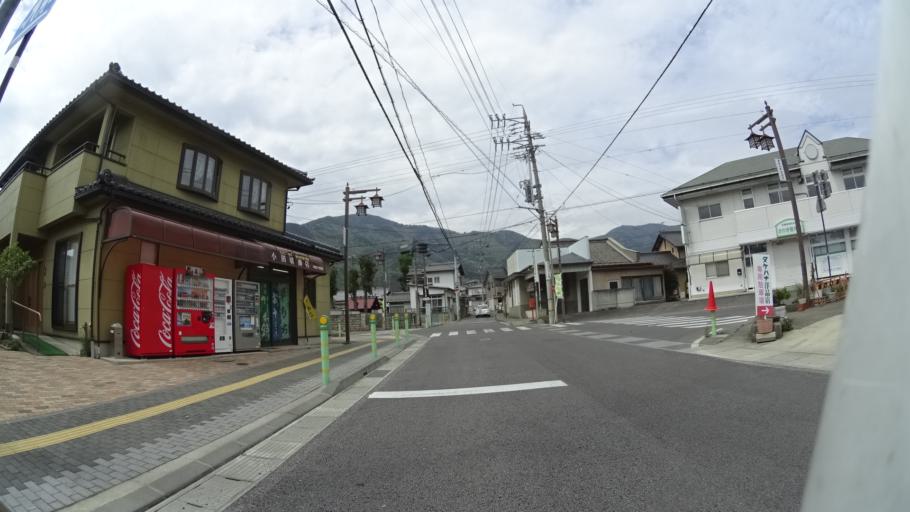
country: JP
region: Nagano
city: Ueda
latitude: 36.4622
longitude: 138.1846
